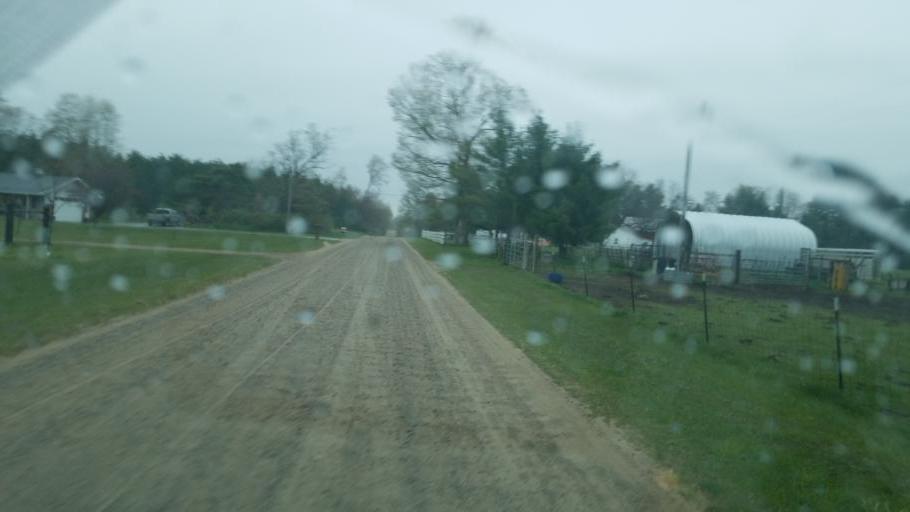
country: US
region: Michigan
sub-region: Mecosta County
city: Canadian Lakes
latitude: 43.5320
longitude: -85.3040
